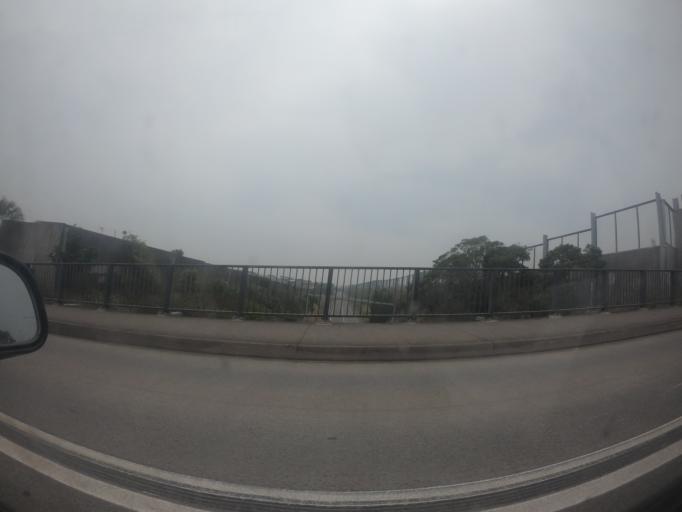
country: AU
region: New South Wales
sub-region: Shellharbour
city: Croom
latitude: -34.5970
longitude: 150.8543
